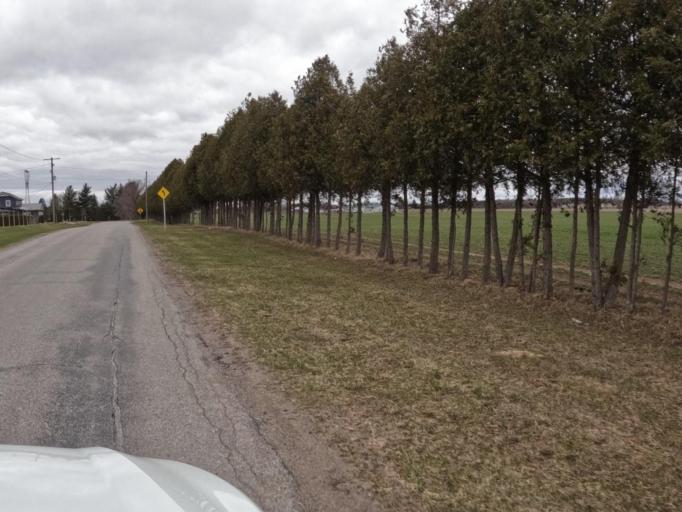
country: CA
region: Ontario
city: Norfolk County
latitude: 42.9602
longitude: -80.3963
